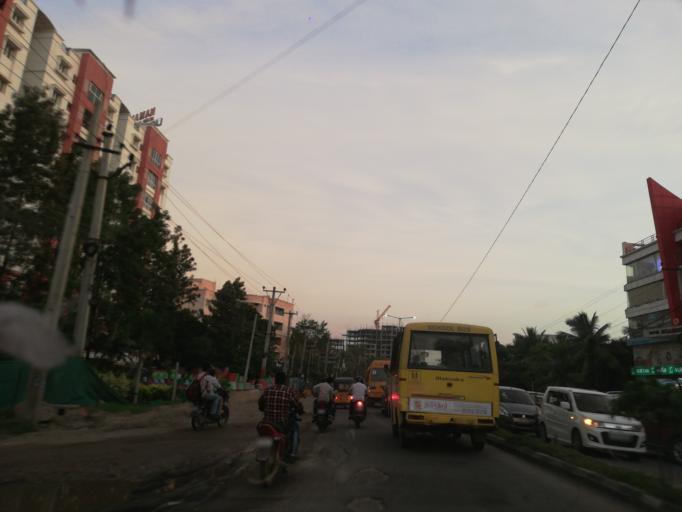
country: IN
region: Telangana
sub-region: Rangareddi
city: Kukatpalli
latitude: 17.5069
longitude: 78.3623
